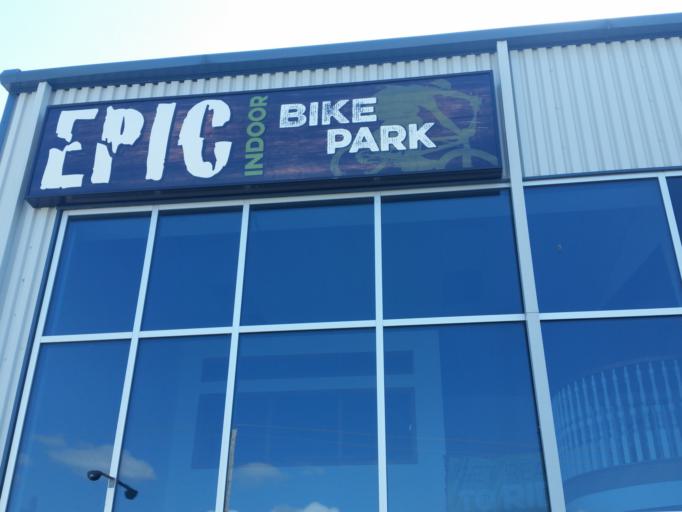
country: CA
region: Ontario
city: Ottawa
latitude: 45.3354
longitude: -75.7125
